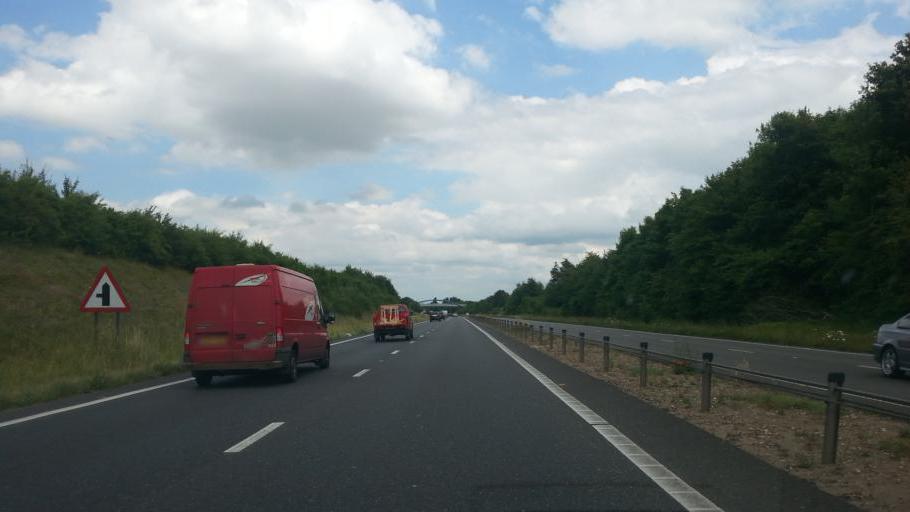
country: GB
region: England
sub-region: Norfolk
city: Snetterton
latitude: 52.5080
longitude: 0.9921
